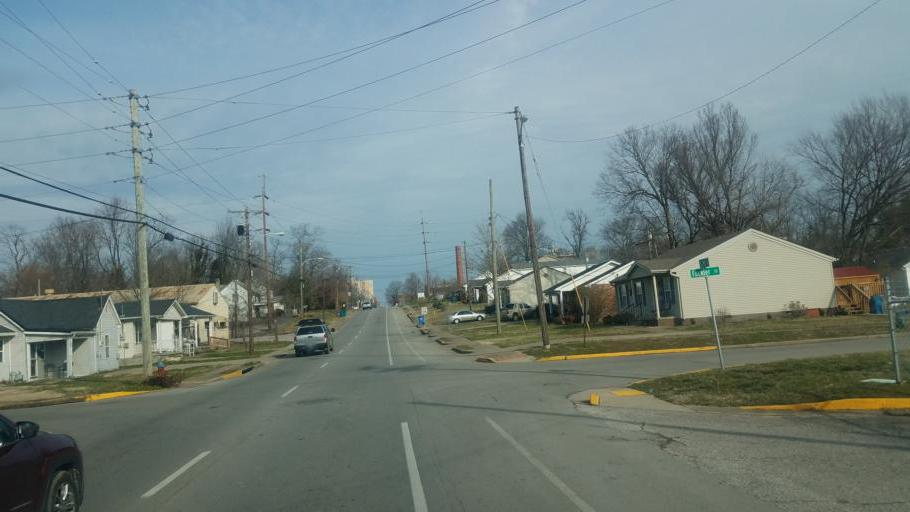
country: US
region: Kentucky
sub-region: Boyle County
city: Danville
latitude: 37.6384
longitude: -84.7732
